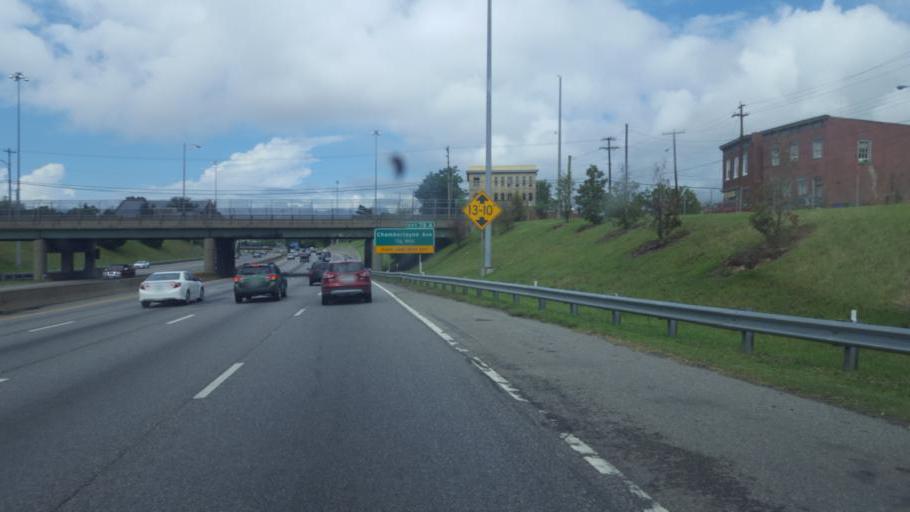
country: US
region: Virginia
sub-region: City of Richmond
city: Richmond
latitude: 37.5501
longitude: -77.4352
